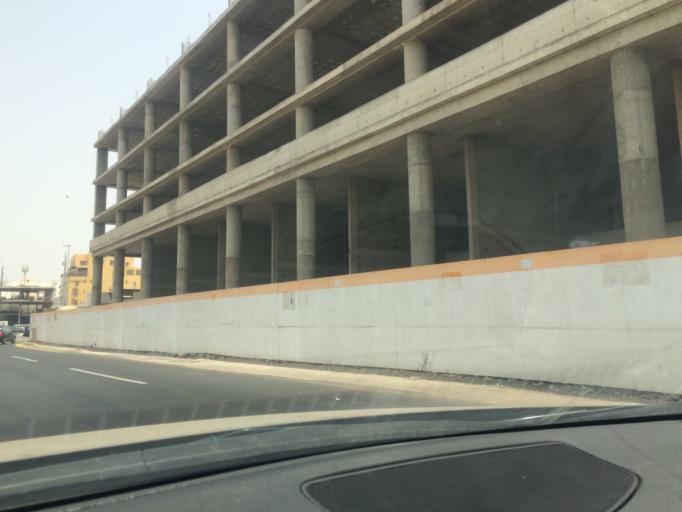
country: SA
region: Makkah
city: Jeddah
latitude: 21.6059
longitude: 39.1196
